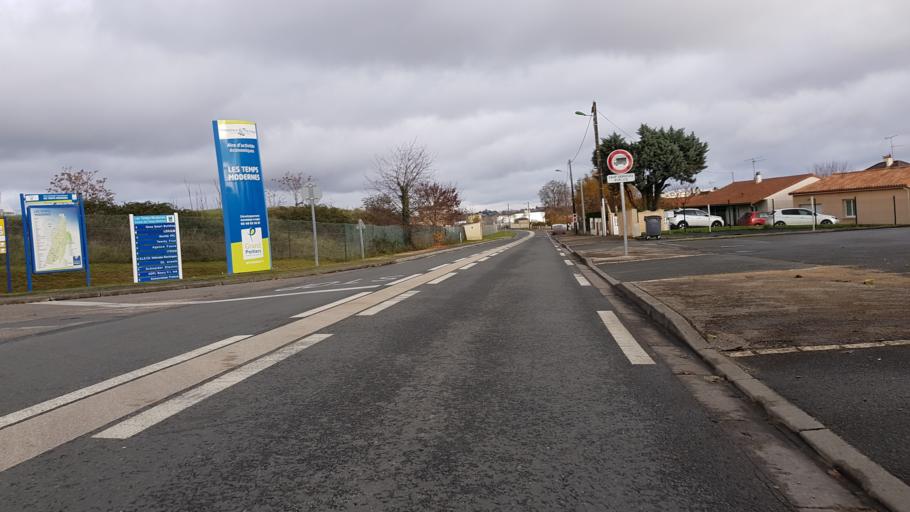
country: FR
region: Poitou-Charentes
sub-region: Departement de la Vienne
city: Chasseneuil-du-Poitou
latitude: 46.6538
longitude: 0.3701
